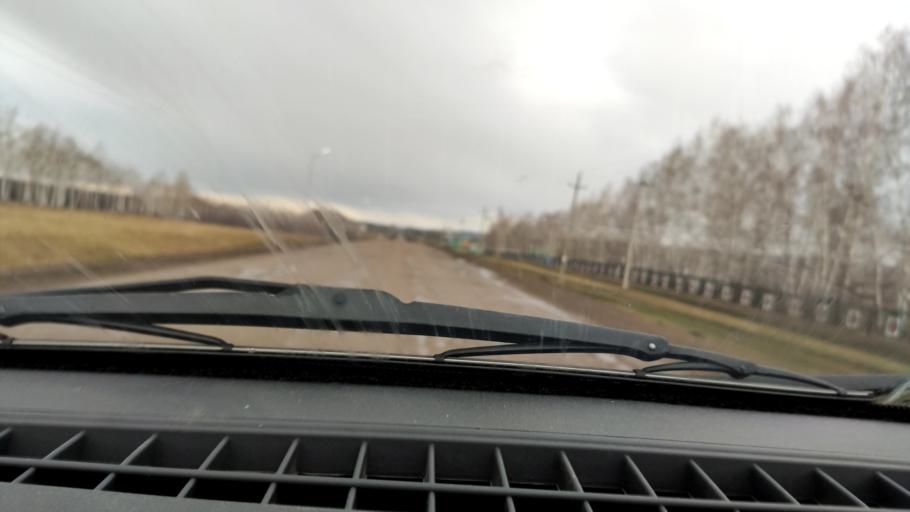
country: RU
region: Bashkortostan
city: Chekmagush
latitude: 55.1161
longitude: 54.8404
